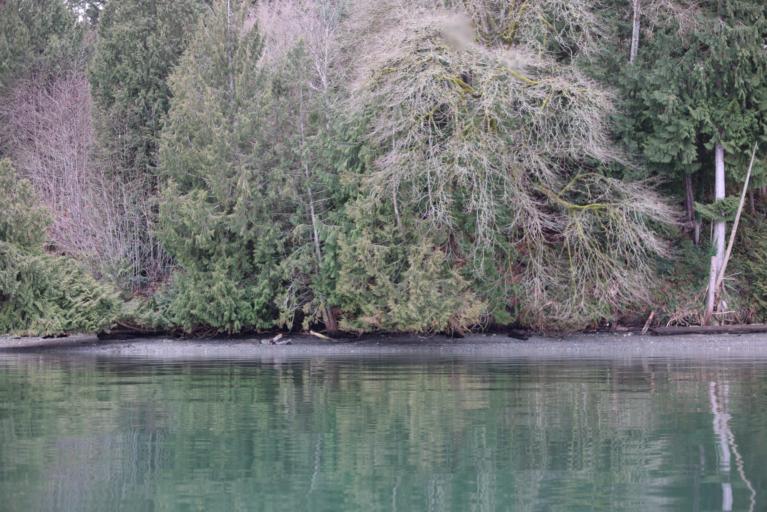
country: CA
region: British Columbia
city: Duncan
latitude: 48.7269
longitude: -123.5733
